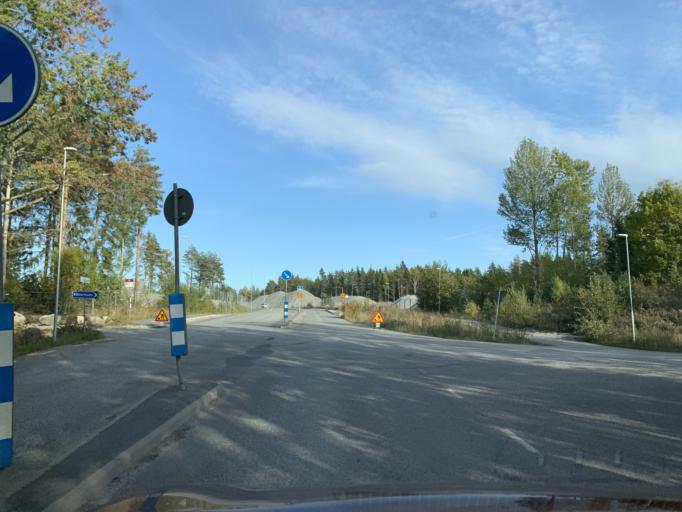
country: SE
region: Stockholm
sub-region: Upplands-Bro Kommun
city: Bro
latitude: 59.5046
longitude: 17.6104
